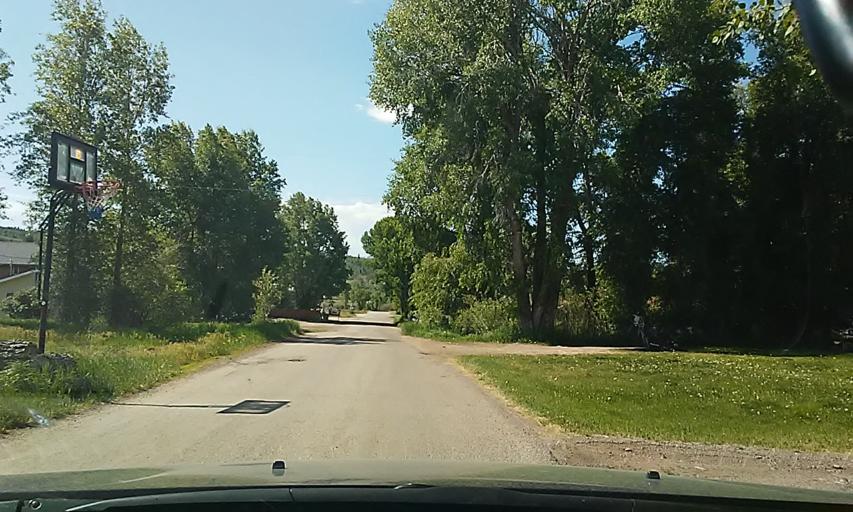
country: US
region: Wyoming
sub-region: Teton County
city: Jackson
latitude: 43.6233
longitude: -110.6239
